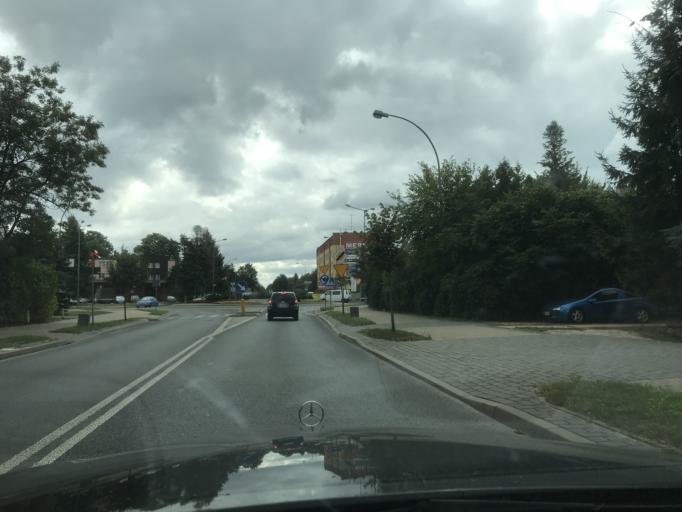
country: PL
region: Lublin Voivodeship
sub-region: Powiat janowski
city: Janow Lubelski
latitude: 50.7013
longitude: 22.4201
